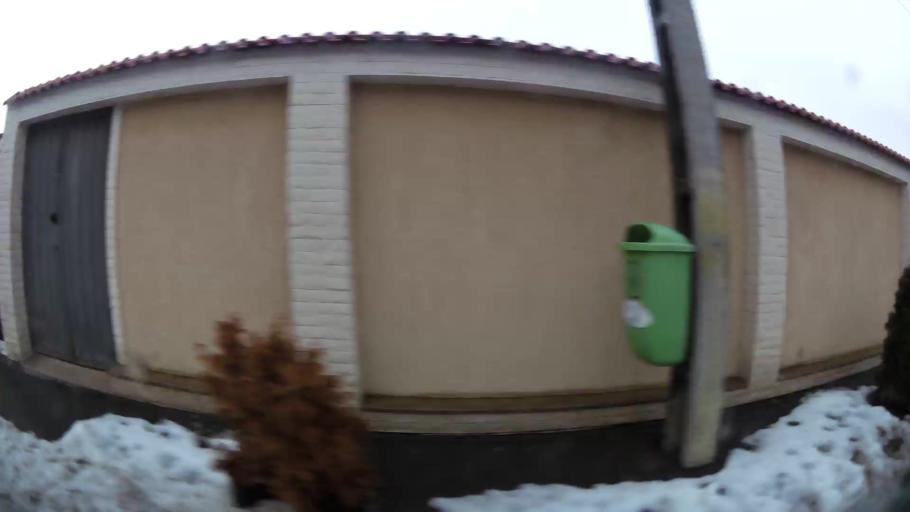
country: RO
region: Ilfov
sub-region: Comuna Mogosoaia
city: Mogosoaia
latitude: 44.5145
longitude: 26.0250
